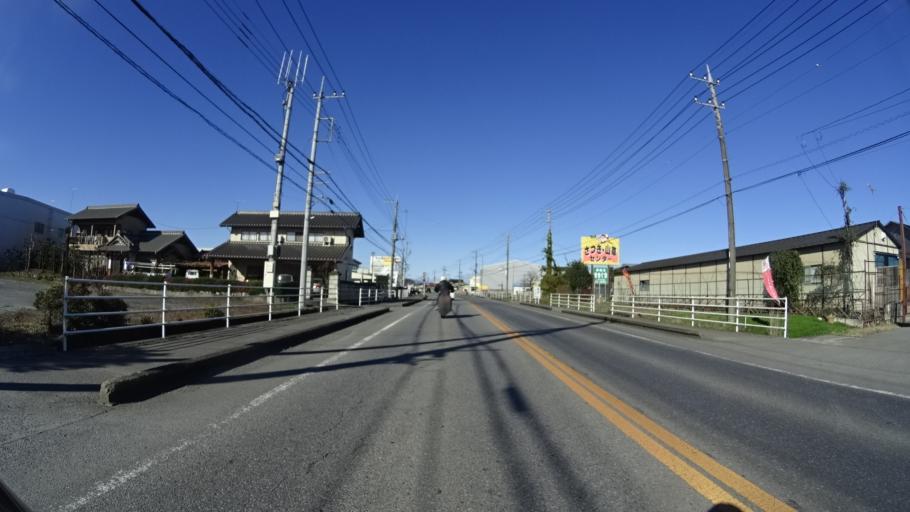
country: JP
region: Tochigi
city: Kanuma
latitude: 36.5234
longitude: 139.7503
